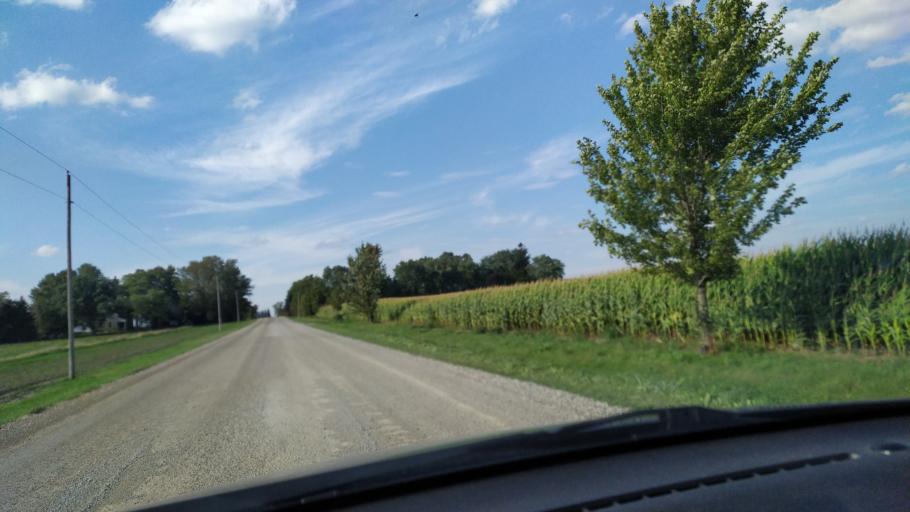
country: CA
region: Ontario
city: Stratford
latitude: 43.2699
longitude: -80.9396
